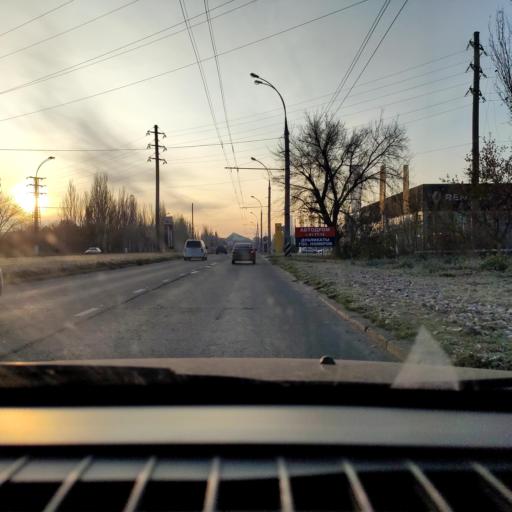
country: RU
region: Samara
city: Tol'yatti
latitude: 53.5465
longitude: 49.2750
